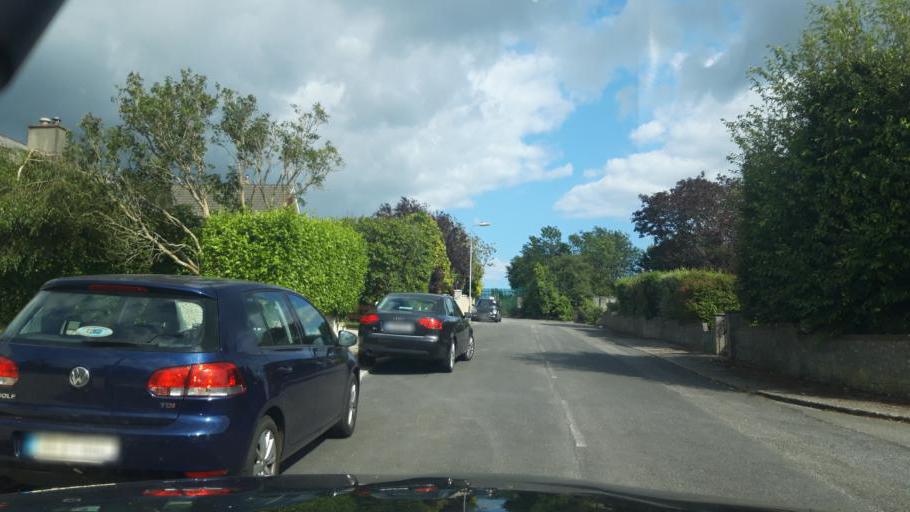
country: IE
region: Munster
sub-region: Waterford
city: Waterford
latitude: 52.2469
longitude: -7.0950
